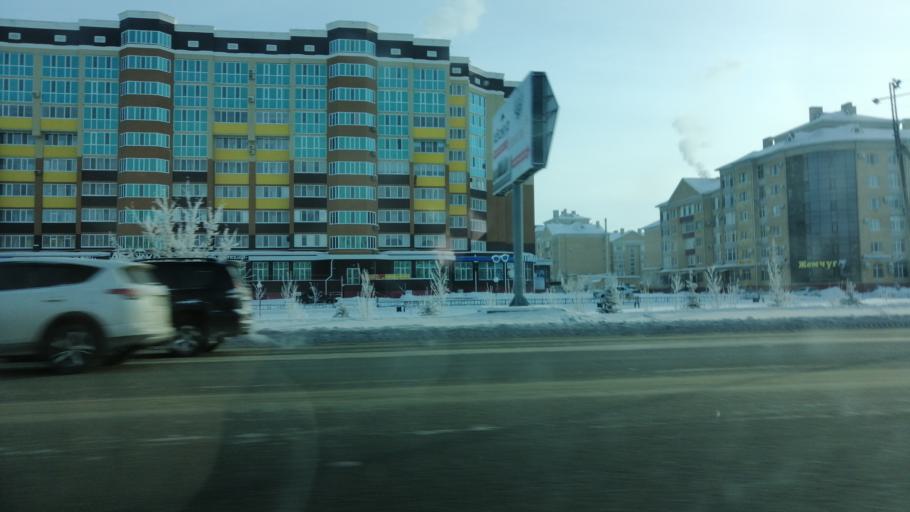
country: KZ
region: Aqtoebe
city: Aqtobe
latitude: 50.2842
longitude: 57.1424
